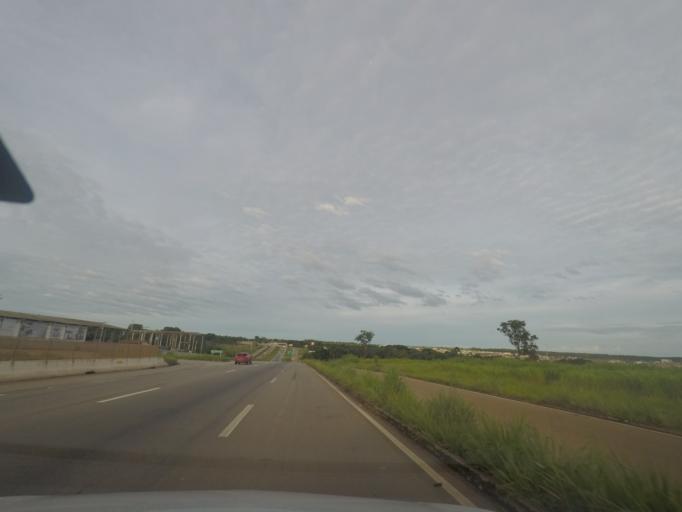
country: BR
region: Goias
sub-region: Trindade
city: Trindade
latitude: -16.7302
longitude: -49.3898
